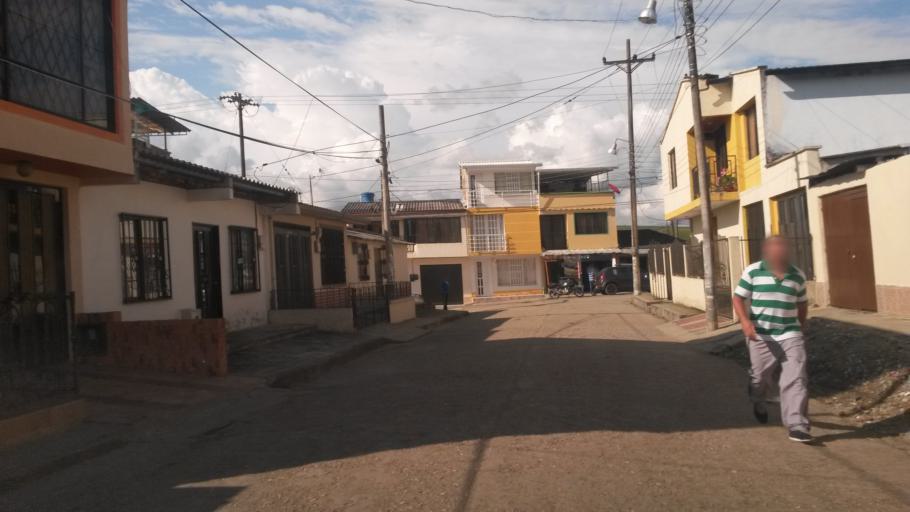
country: CO
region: Cauca
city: Popayan
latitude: 2.3514
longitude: -76.6789
